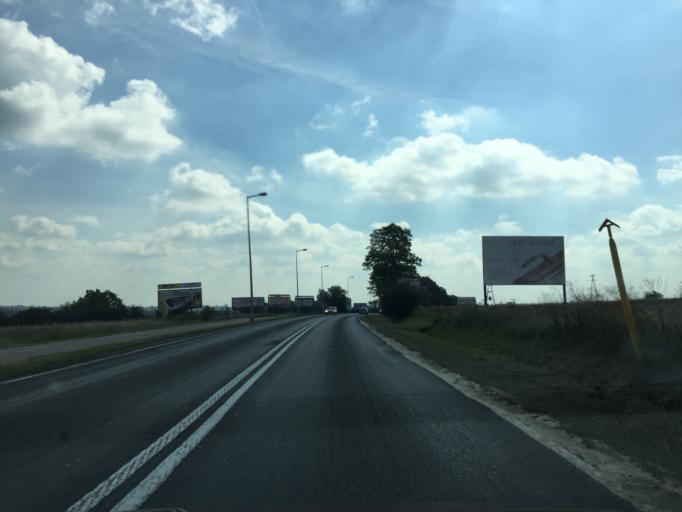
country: PL
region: Greater Poland Voivodeship
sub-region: Kalisz
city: Kalisz
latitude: 51.7684
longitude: 18.0475
